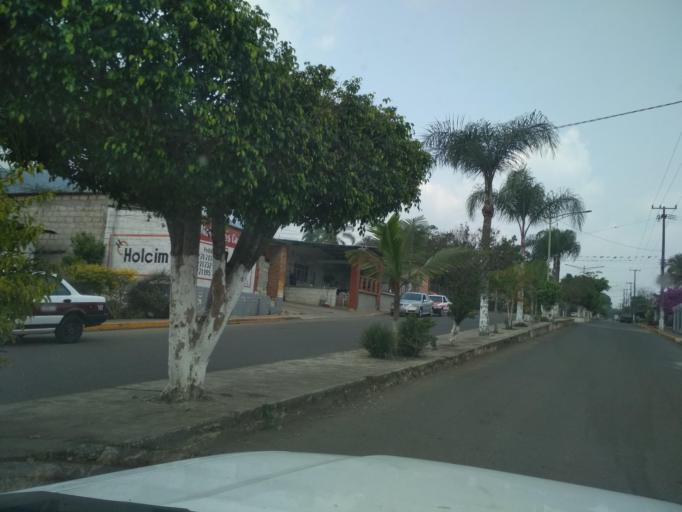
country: MX
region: Veracruz
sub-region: Cordoba
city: Fredepo
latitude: 18.8526
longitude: -96.9819
